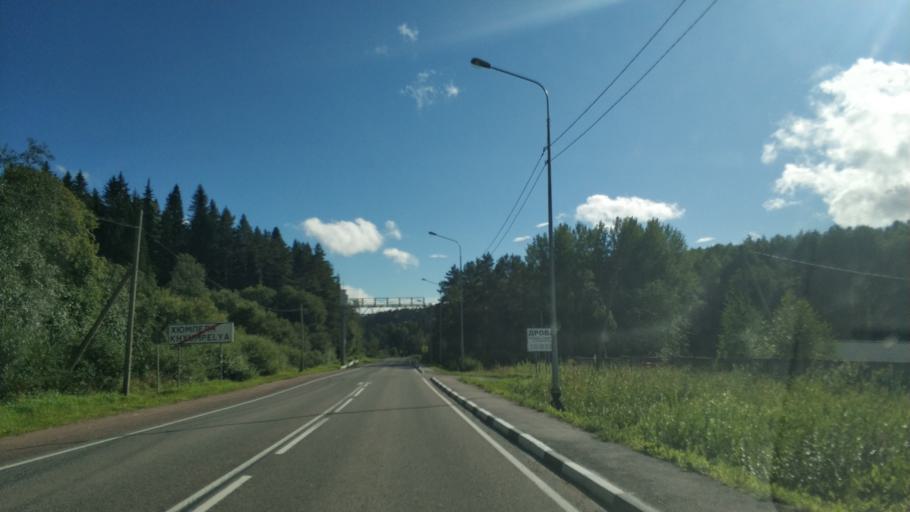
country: RU
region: Republic of Karelia
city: Sortavala
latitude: 61.6745
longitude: 30.6548
